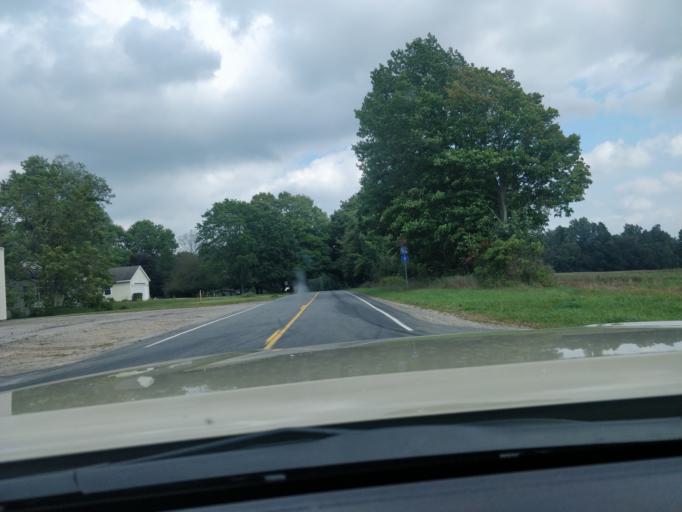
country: US
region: Michigan
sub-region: Kent County
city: Lowell
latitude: 42.8859
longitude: -85.2923
